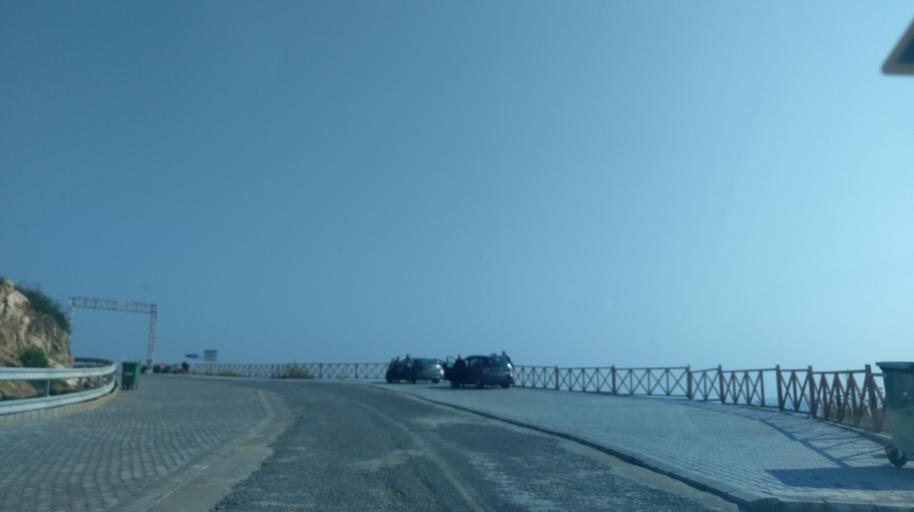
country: CY
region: Ammochostos
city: Rizokarpaso
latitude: 35.6440
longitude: 34.5578
